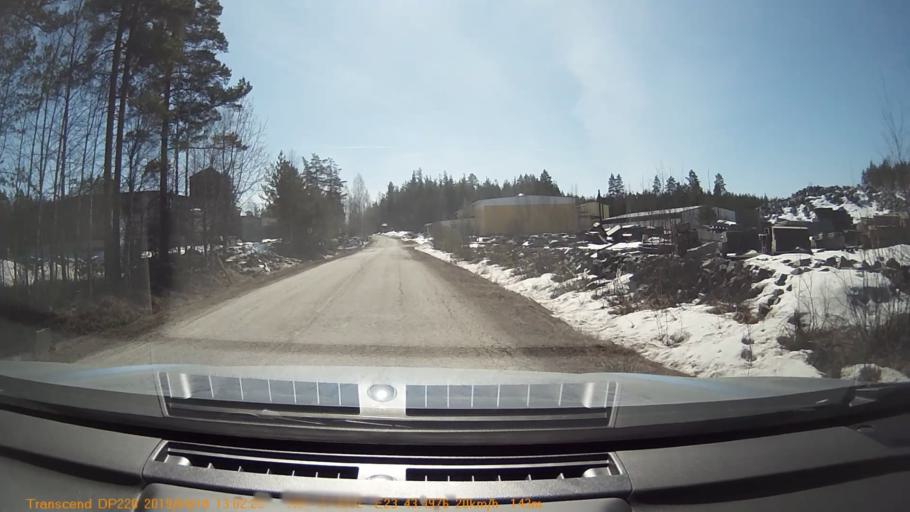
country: FI
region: Pirkanmaa
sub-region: Tampere
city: Kuru
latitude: 61.8607
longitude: 23.7250
